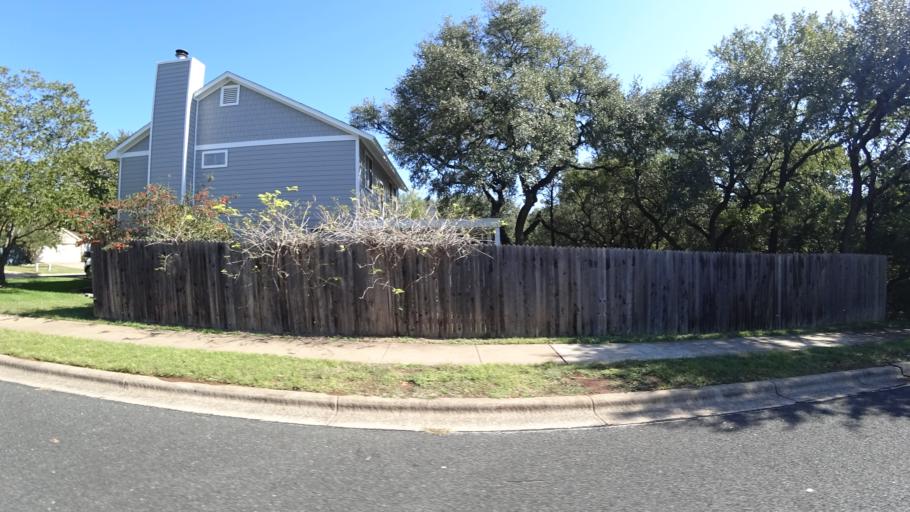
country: US
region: Texas
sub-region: Travis County
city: Shady Hollow
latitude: 30.2149
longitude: -97.8724
